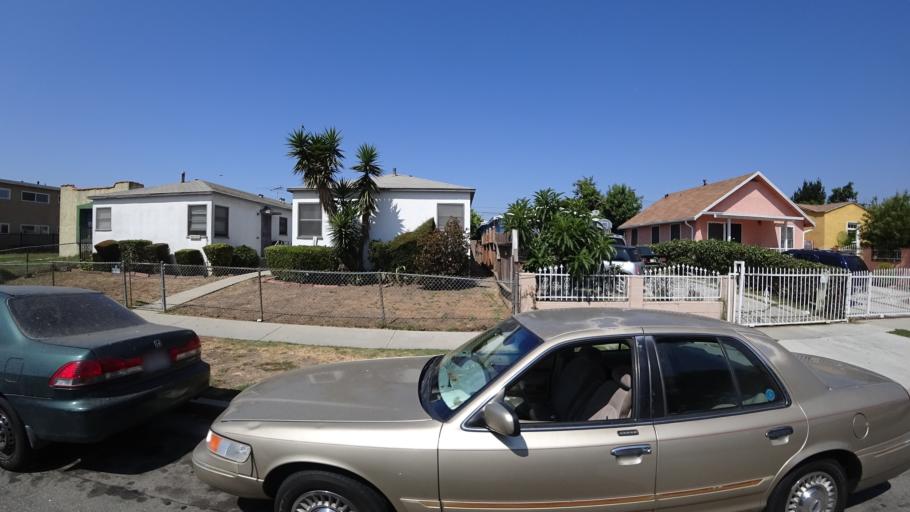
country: US
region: California
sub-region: Los Angeles County
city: Westmont
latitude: 33.9322
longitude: -118.2931
